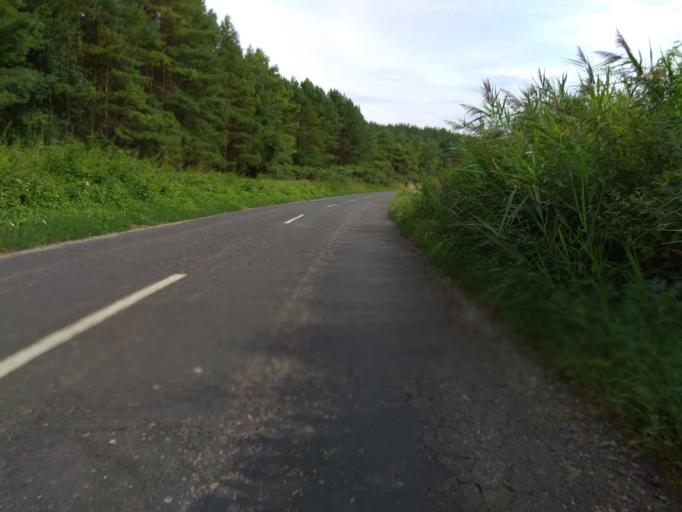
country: HU
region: Heves
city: Tarnalelesz
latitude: 48.0382
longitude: 20.2507
